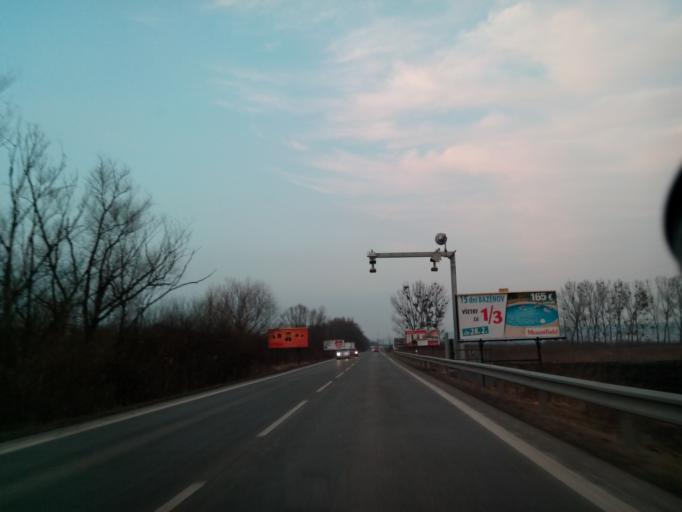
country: SK
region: Kosicky
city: Kosice
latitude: 48.6589
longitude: 21.2710
